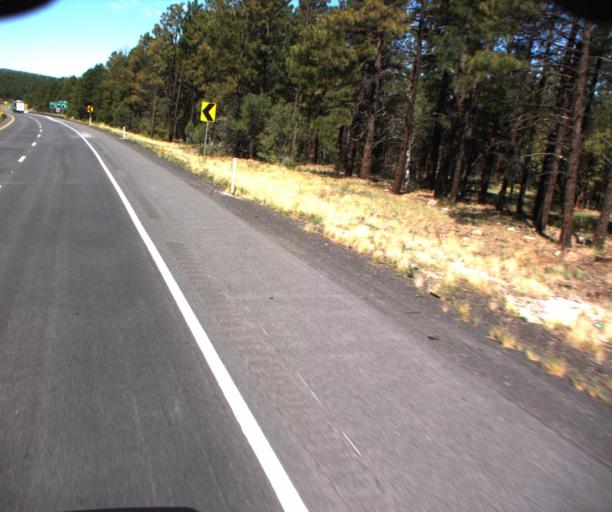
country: US
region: Arizona
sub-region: Coconino County
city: Williams
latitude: 35.2219
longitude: -112.2736
